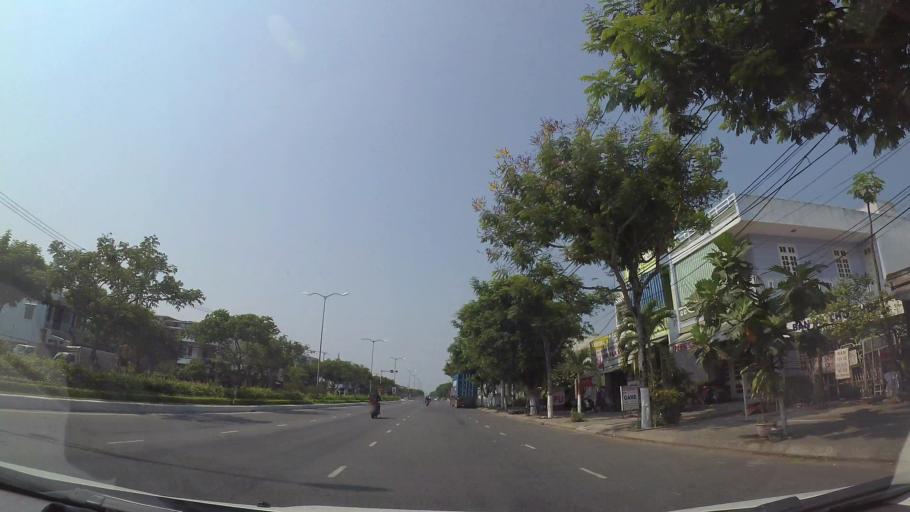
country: VN
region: Da Nang
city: Ngu Hanh Son
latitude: 16.0119
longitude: 108.2564
